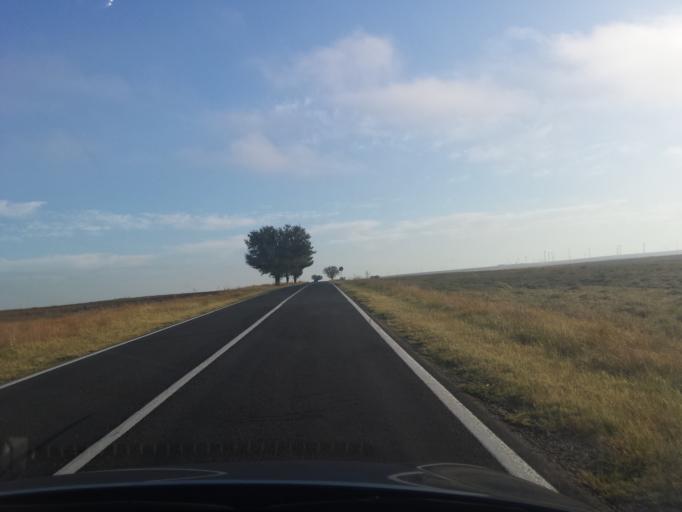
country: RO
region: Constanta
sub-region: Comuna Saraiu
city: Saraiu
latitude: 44.7294
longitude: 28.1675
